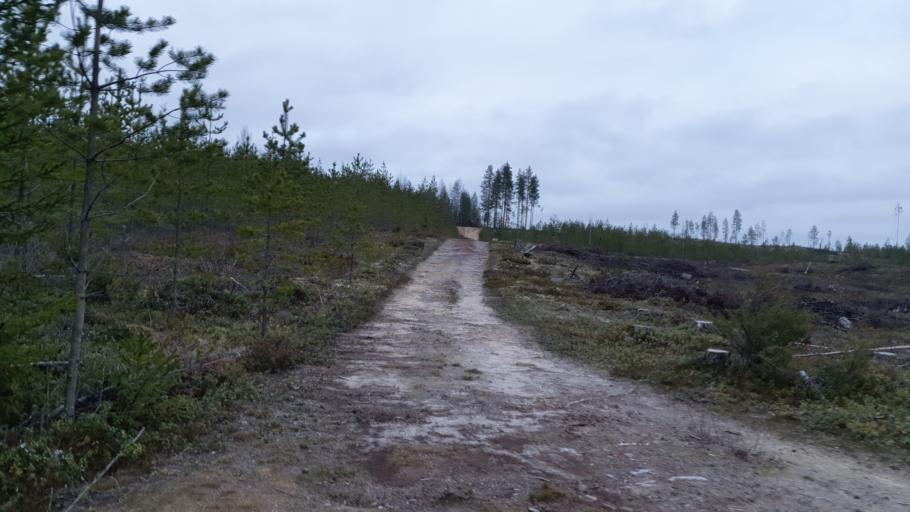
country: FI
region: Kainuu
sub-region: Kehys-Kainuu
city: Kuhmo
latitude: 64.1470
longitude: 29.4092
